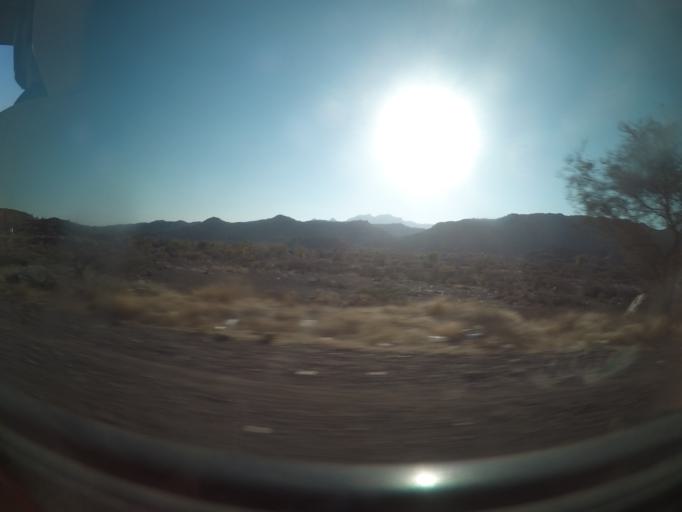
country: YE
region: Lahij
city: Habil ar Raydah
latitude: 13.6572
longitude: 44.8431
